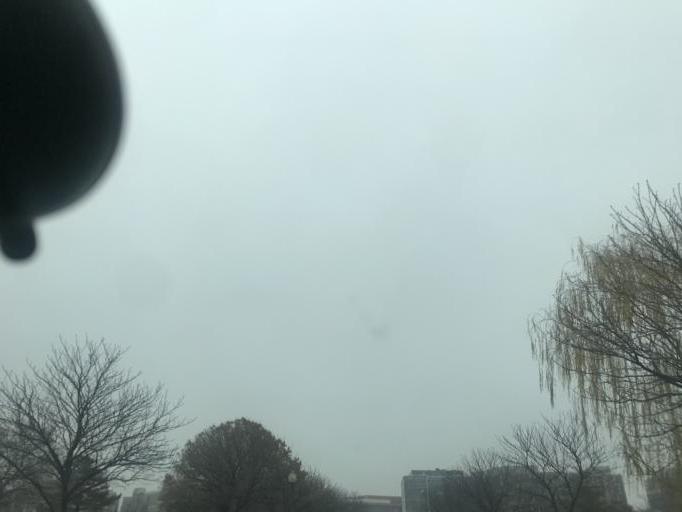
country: US
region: Washington, D.C.
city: Washington, D.C.
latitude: 38.8779
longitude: -77.0305
